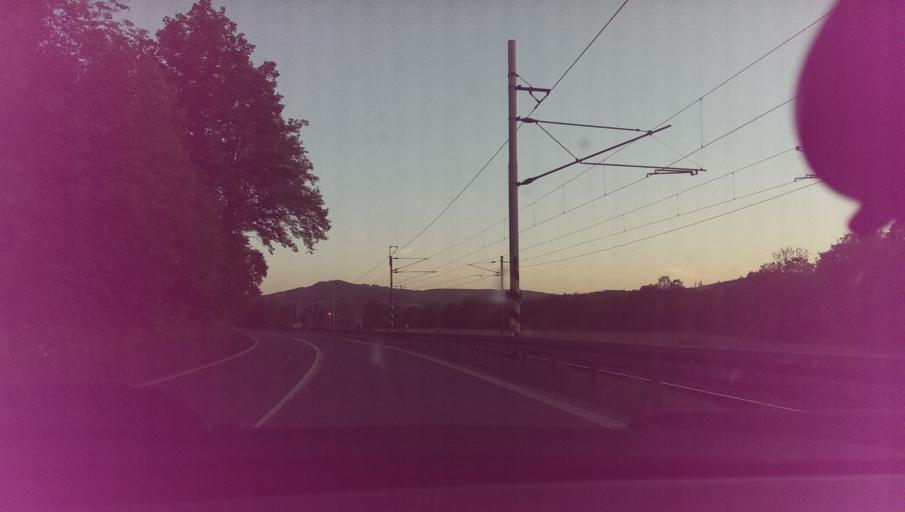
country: CZ
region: Zlin
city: Jablunka
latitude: 49.3959
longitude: 17.9520
